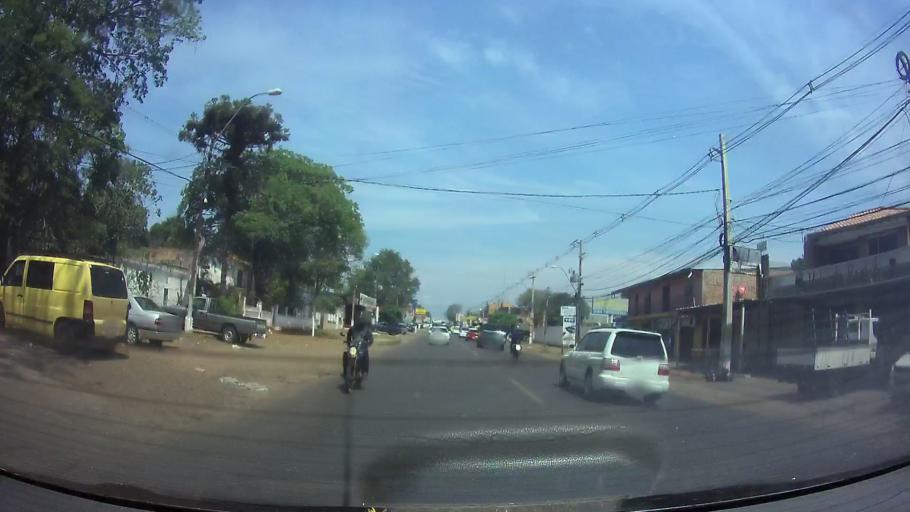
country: PY
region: Central
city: Capiata
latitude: -25.3676
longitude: -57.4810
